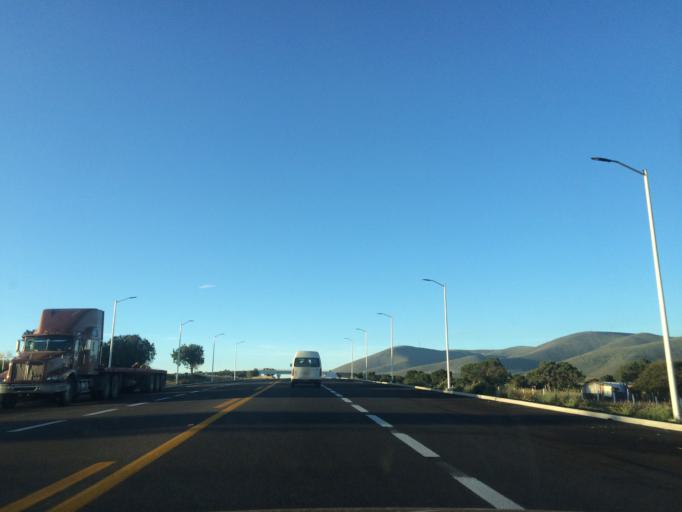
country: MX
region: Puebla
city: Cuacnopalan
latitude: 18.7630
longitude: -97.4831
